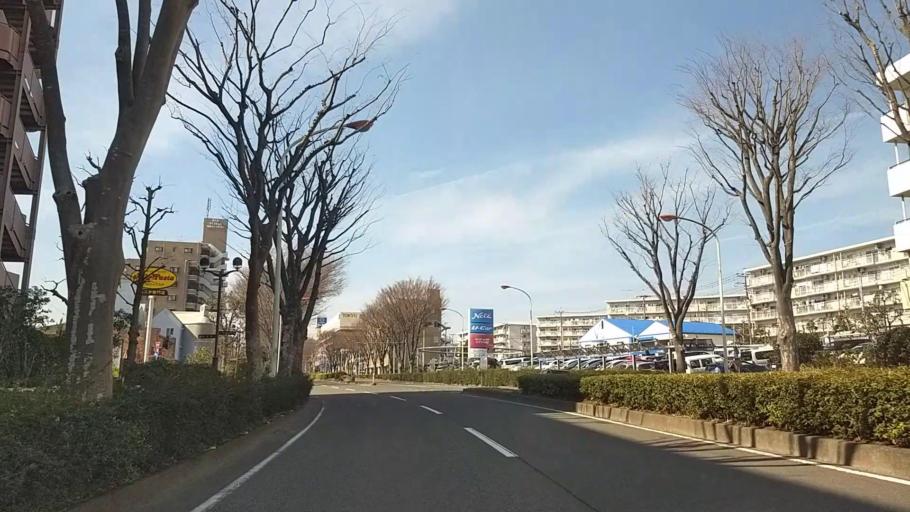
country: JP
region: Kanagawa
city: Fujisawa
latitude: 35.3692
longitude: 139.4460
